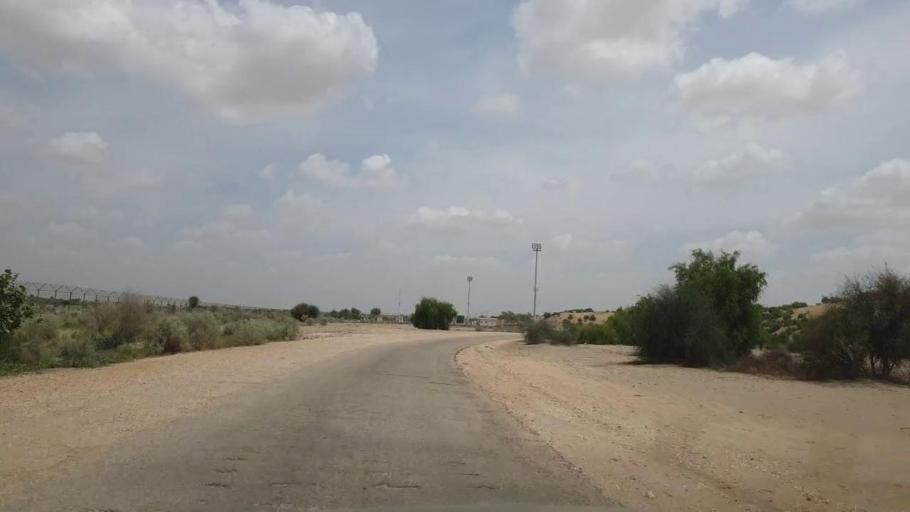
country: PK
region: Sindh
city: Kot Diji
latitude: 27.2016
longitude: 69.1496
